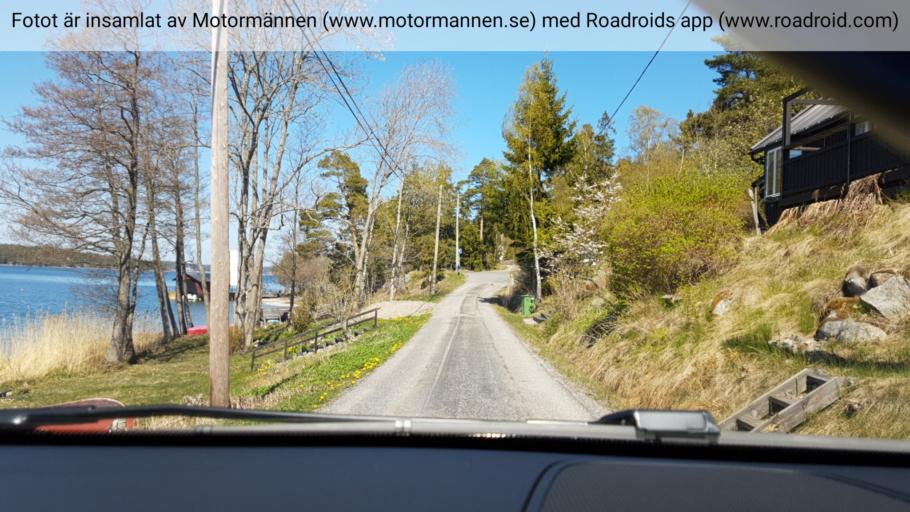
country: SE
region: Stockholm
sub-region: Haninge Kommun
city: Jordbro
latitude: 59.0177
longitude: 18.0928
